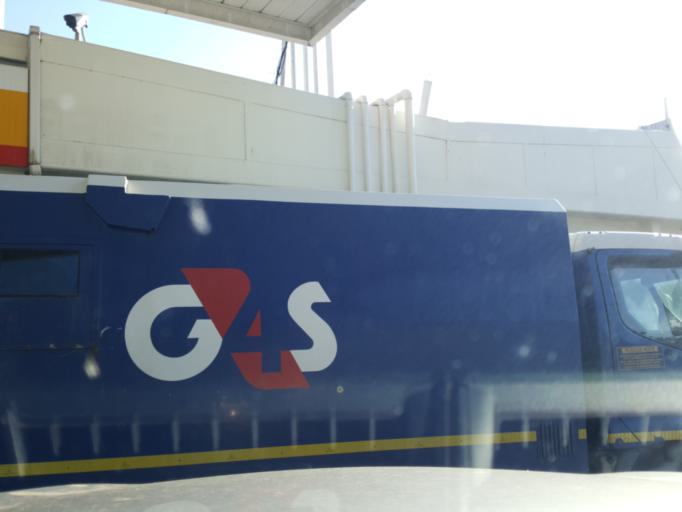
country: ZA
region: Eastern Cape
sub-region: Cacadu District Municipality
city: Grahamstown
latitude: -33.3126
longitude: 26.5299
